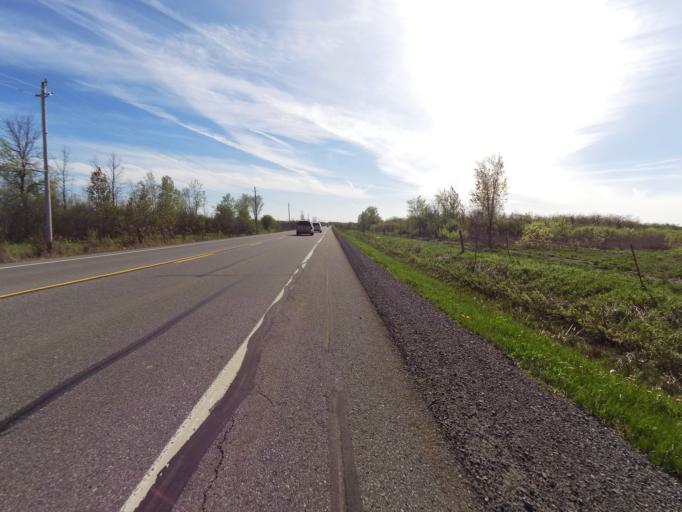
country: CA
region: Ontario
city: Ottawa
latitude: 45.3036
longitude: -75.6631
